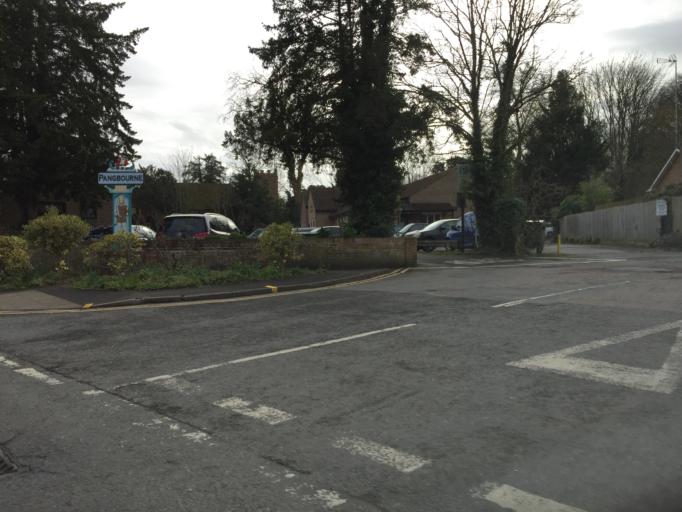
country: GB
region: England
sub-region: West Berkshire
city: Pangbourne
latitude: 51.4845
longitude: -1.0884
